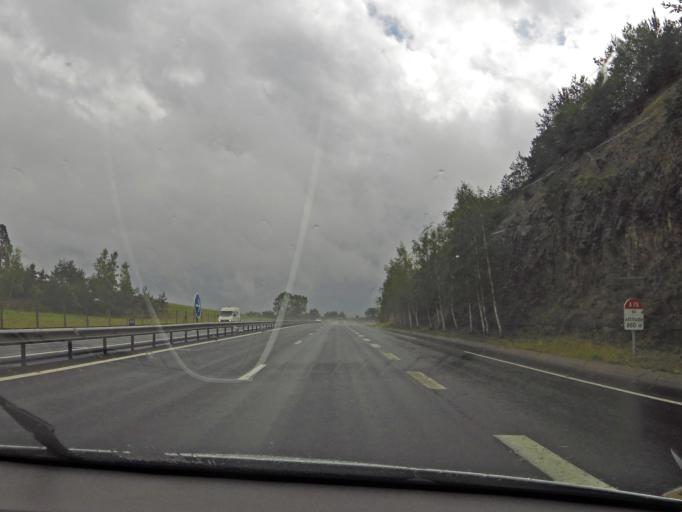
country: FR
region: Auvergne
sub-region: Departement du Cantal
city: Saint-Flour
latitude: 45.0485
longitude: 3.1141
